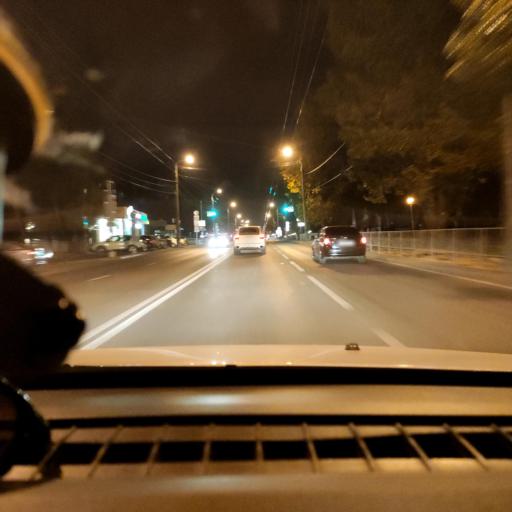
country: RU
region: Samara
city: Samara
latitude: 53.2369
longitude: 50.2248
